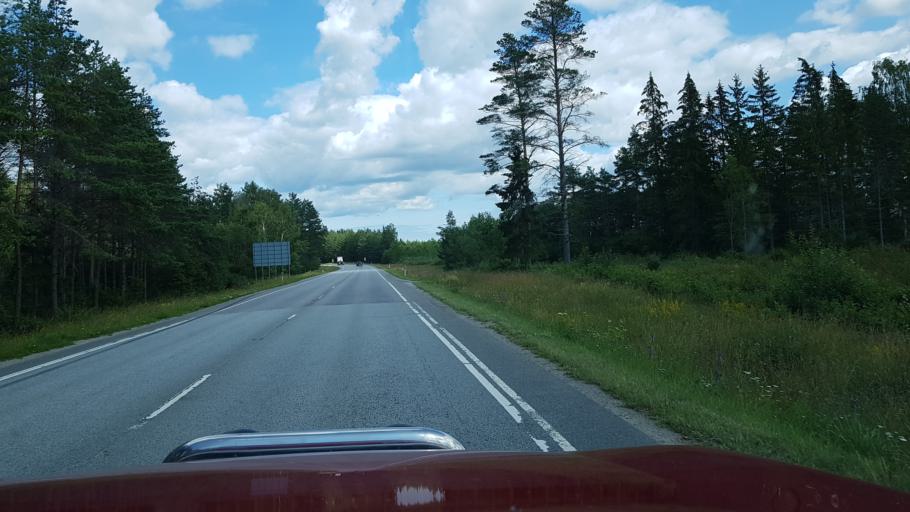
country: EE
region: Laeaene-Virumaa
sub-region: Someru vald
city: Someru
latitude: 59.3344
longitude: 26.4071
